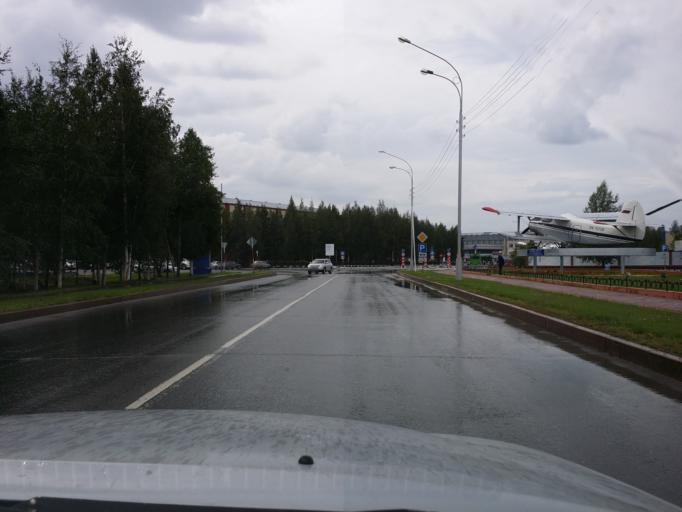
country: RU
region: Khanty-Mansiyskiy Avtonomnyy Okrug
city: Nizhnevartovsk
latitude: 60.9502
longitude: 76.5011
